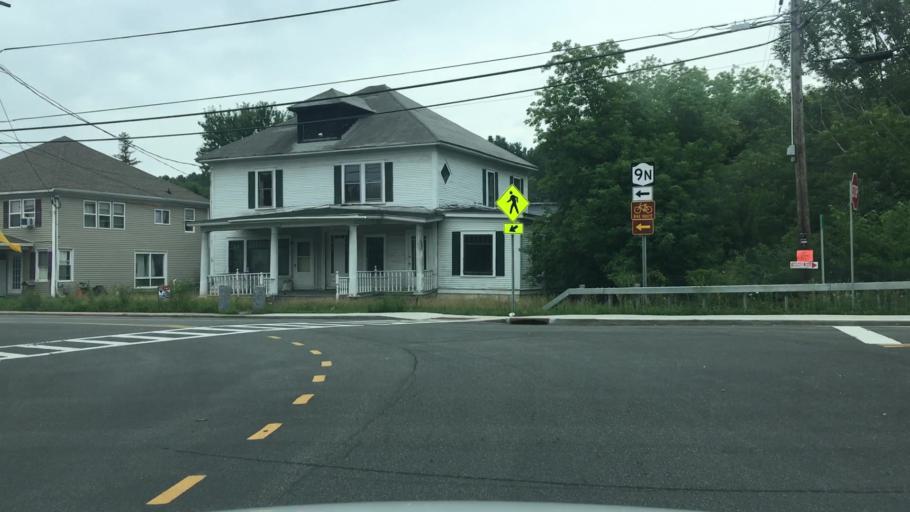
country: US
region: New York
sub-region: Clinton County
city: Peru
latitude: 44.4384
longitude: -73.6786
